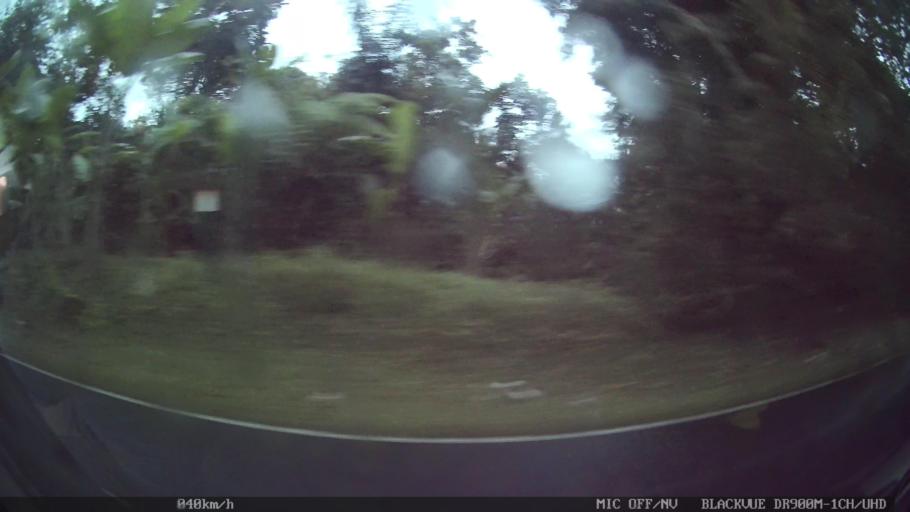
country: ID
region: Bali
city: Banjar Taro Kelod
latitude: -8.3610
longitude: 115.2721
